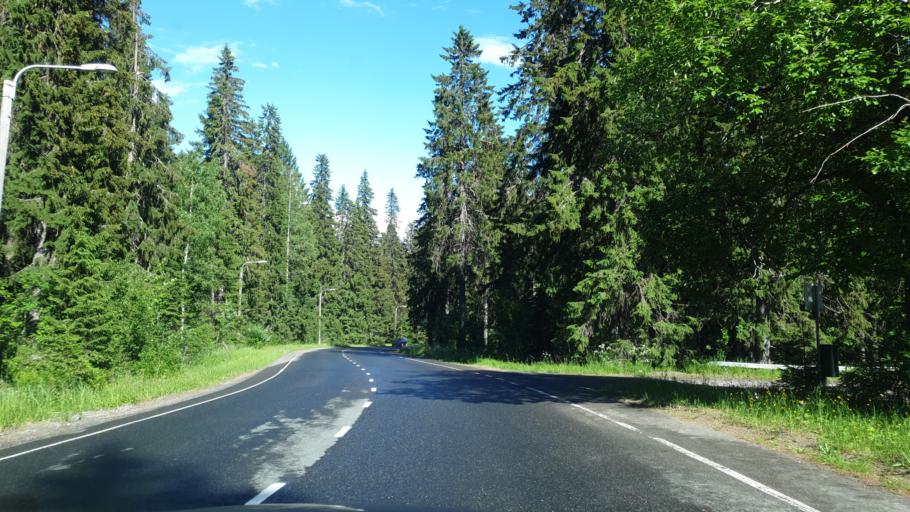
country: FI
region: Northern Savo
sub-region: Kuopio
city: Kuopio
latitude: 62.9089
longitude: 27.6586
